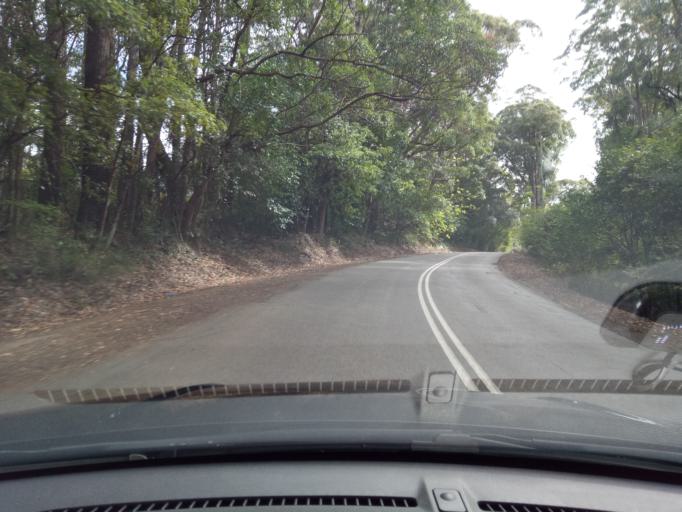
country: AU
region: New South Wales
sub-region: Gosford Shire
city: Holgate
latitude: -33.3944
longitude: 151.4031
